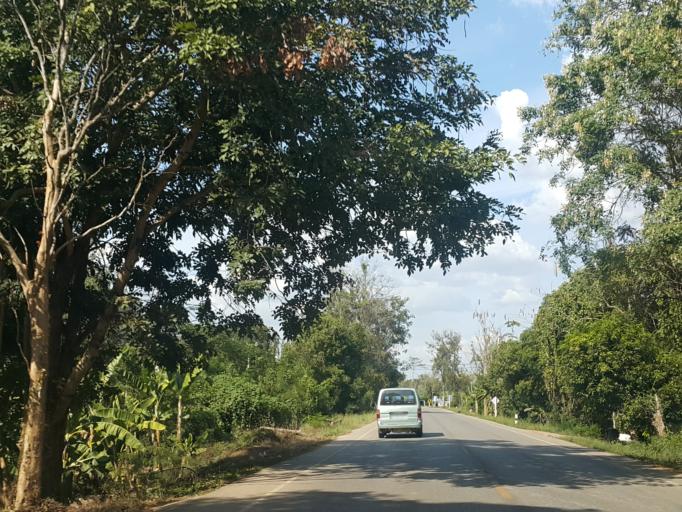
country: TH
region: Sukhothai
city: Sawankhalok
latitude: 17.2604
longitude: 99.8363
